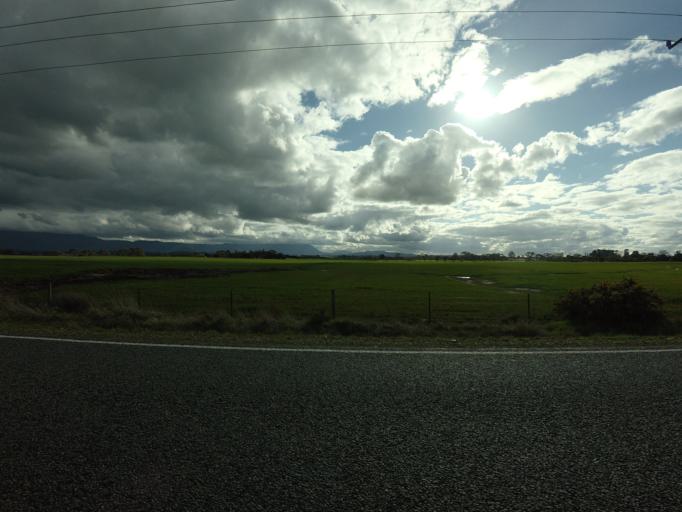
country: AU
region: Tasmania
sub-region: Northern Midlands
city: Longford
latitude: -41.7277
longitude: 147.0878
